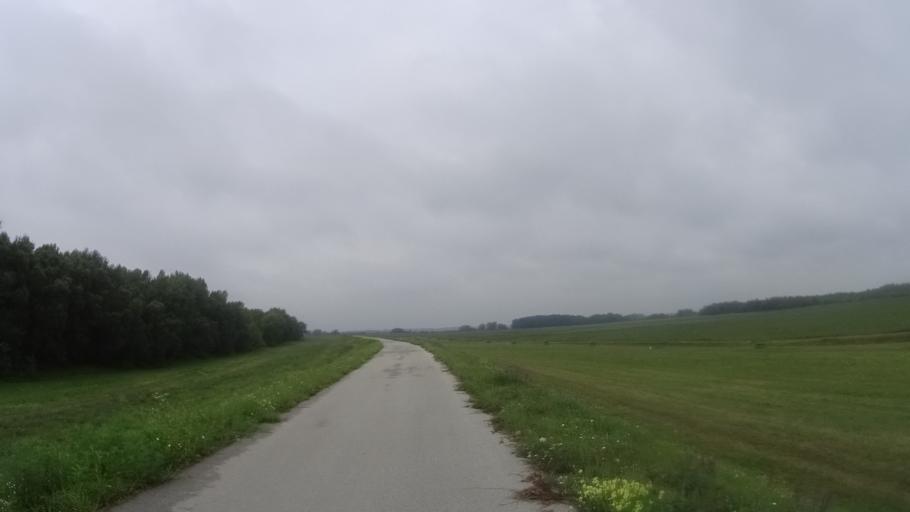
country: HU
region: Komarom-Esztergom
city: Almasfuzito
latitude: 47.7472
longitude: 18.2164
